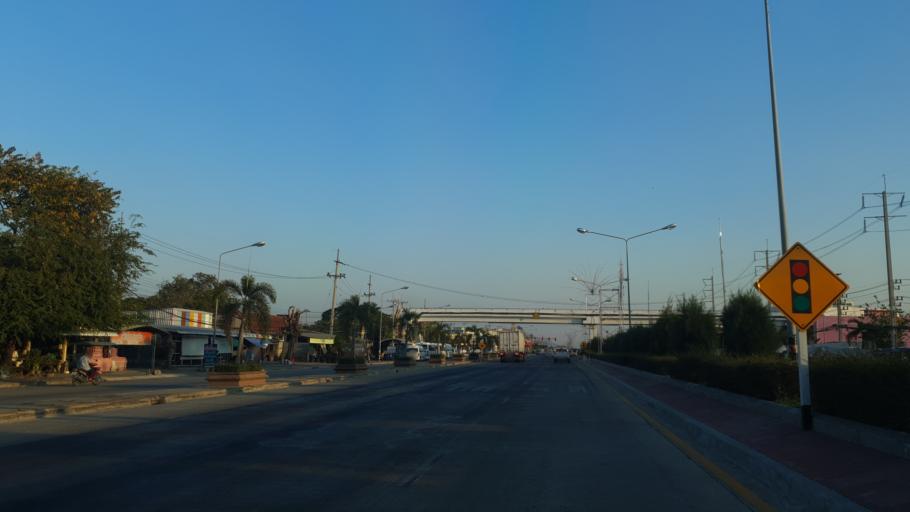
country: TH
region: Kamphaeng Phet
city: Khanu Woralaksaburi
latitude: 16.0012
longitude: 99.8032
